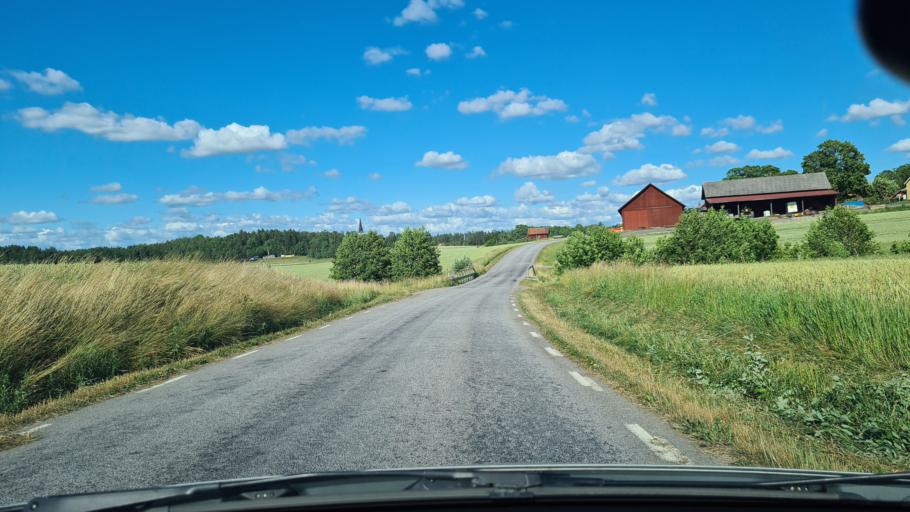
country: SE
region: Soedermanland
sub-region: Nykopings Kommun
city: Olstorp
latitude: 58.8271
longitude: 16.5089
